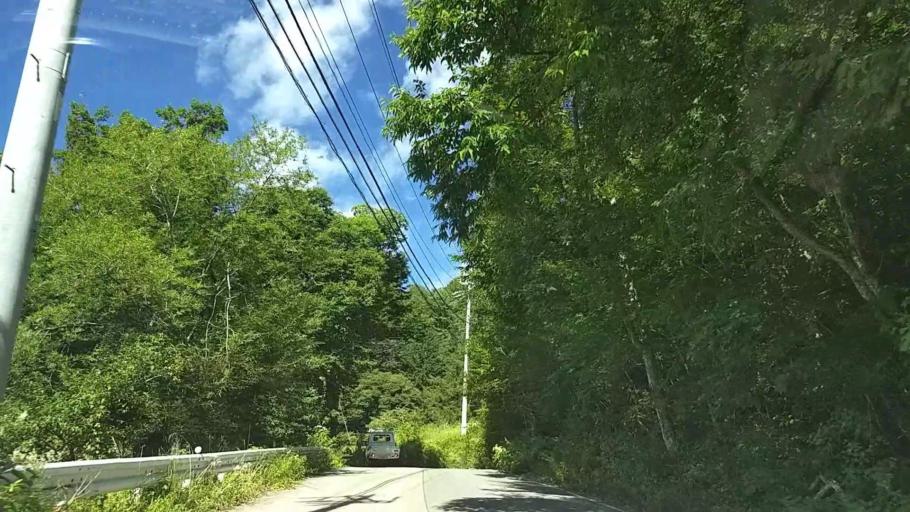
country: JP
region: Nagano
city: Matsumoto
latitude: 36.2099
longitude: 138.1026
